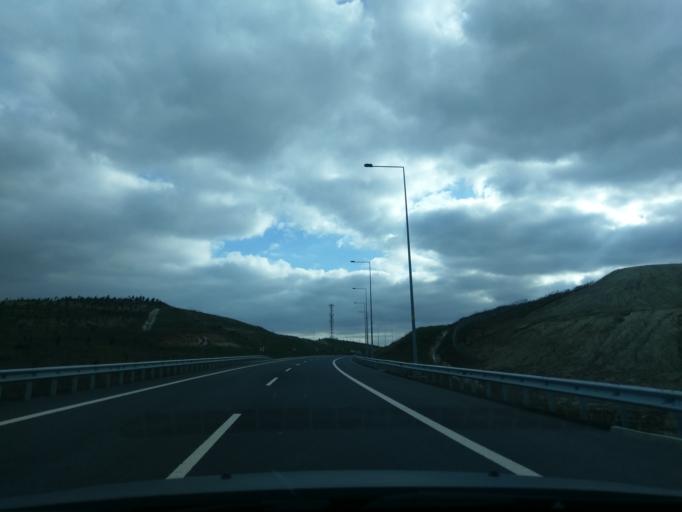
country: TR
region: Istanbul
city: Kemerburgaz
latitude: 41.2344
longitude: 28.8393
